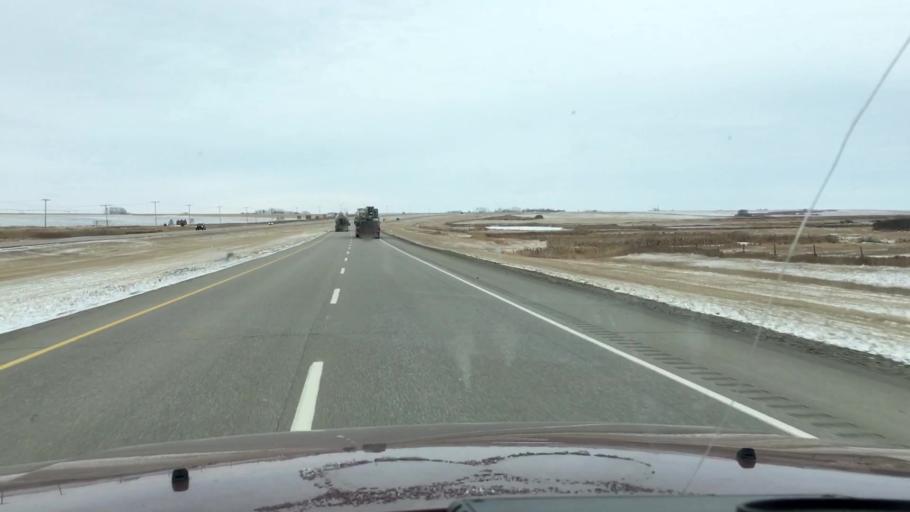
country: CA
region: Saskatchewan
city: Watrous
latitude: 51.2406
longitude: -105.9653
